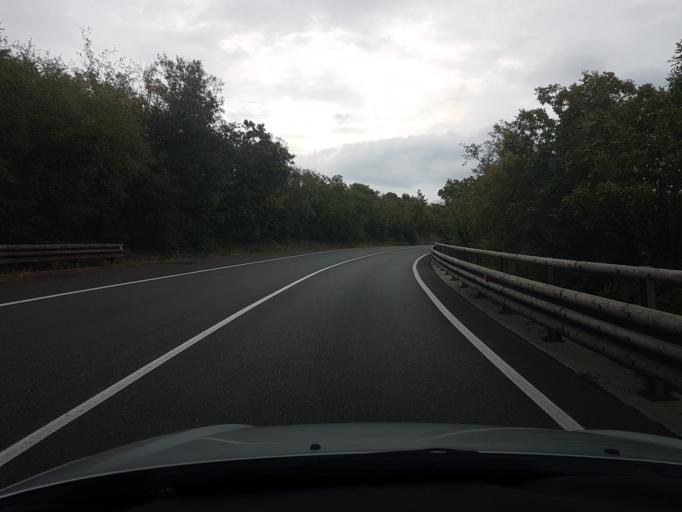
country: IT
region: Friuli Venezia Giulia
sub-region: Provincia di Trieste
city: Duino
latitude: 45.7865
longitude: 13.5936
